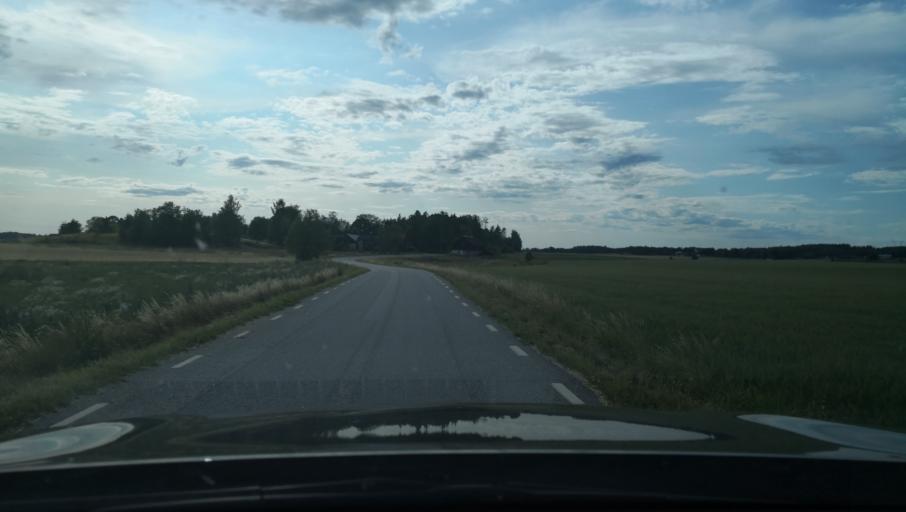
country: SE
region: Uppsala
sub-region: Enkopings Kommun
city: Orsundsbro
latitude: 59.6900
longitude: 17.3671
